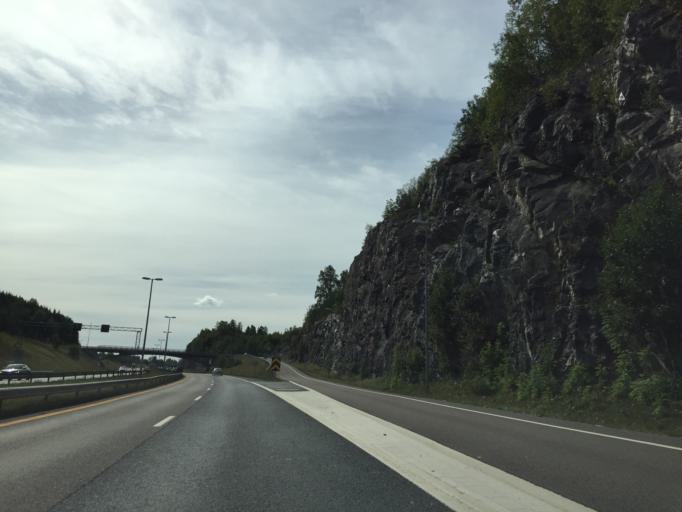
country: NO
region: Akershus
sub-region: As
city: As
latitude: 59.6916
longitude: 10.7334
